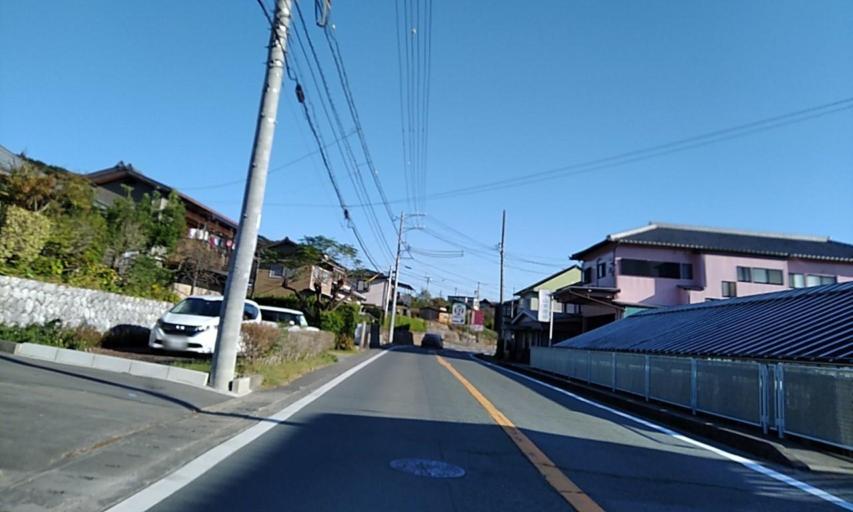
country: JP
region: Shizuoka
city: Hamakita
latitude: 34.8362
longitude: 137.6641
